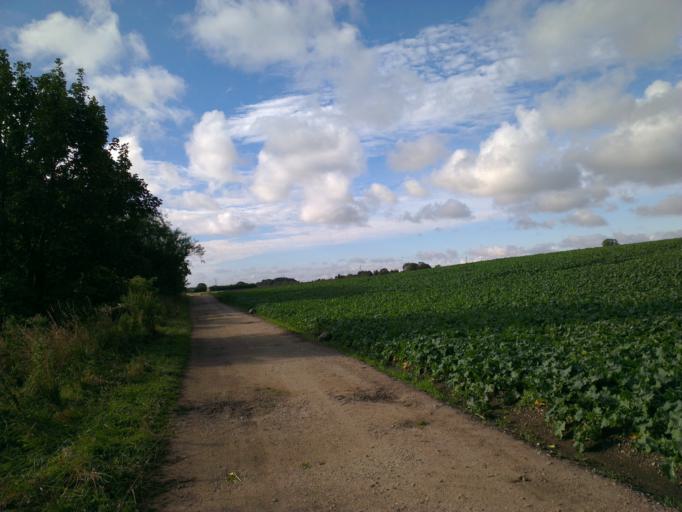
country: DK
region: Capital Region
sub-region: Frederikssund Kommune
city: Frederikssund
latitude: 55.8075
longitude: 12.0861
